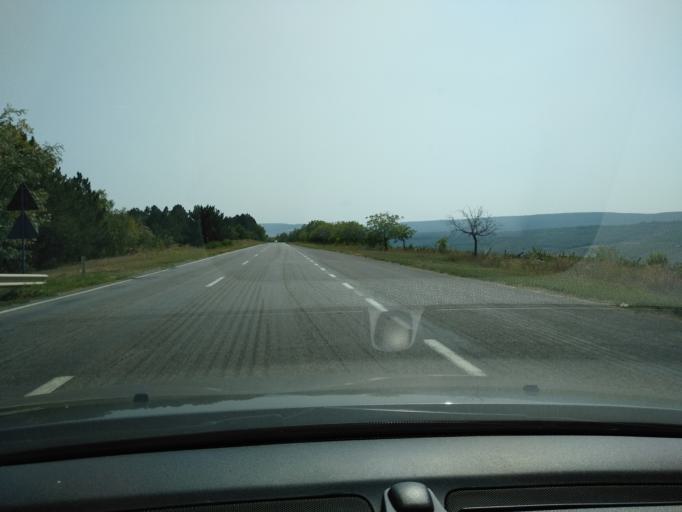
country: MD
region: Nisporeni
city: Nisporeni
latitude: 47.0708
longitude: 28.2710
